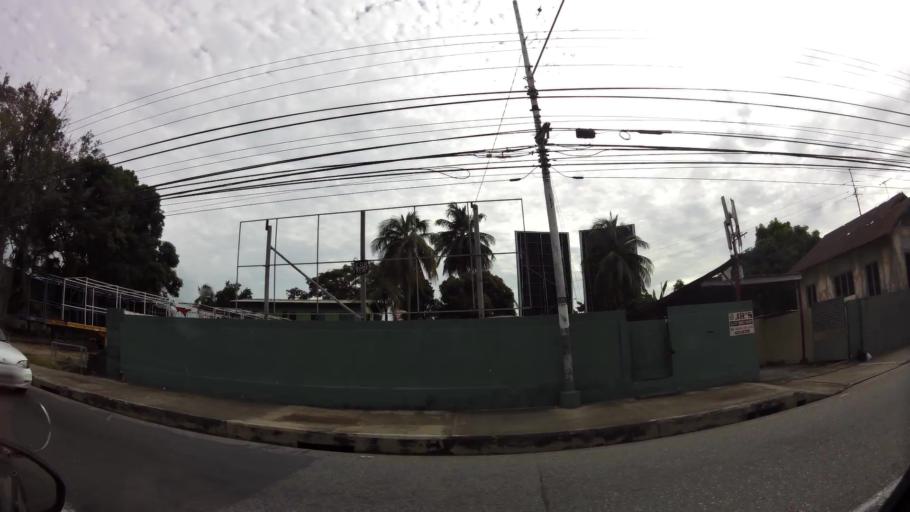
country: TT
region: City of Port of Spain
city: Mucurapo
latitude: 10.6684
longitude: -61.5361
